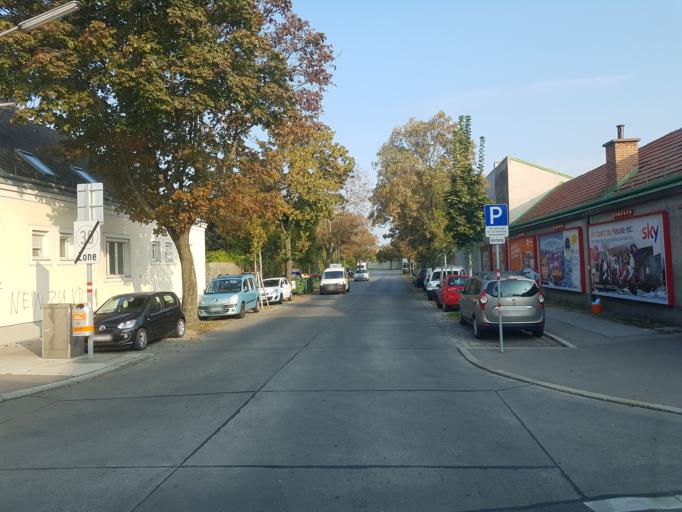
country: AT
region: Lower Austria
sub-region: Politischer Bezirk Wien-Umgebung
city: Gerasdorf bei Wien
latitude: 48.2635
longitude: 16.4410
